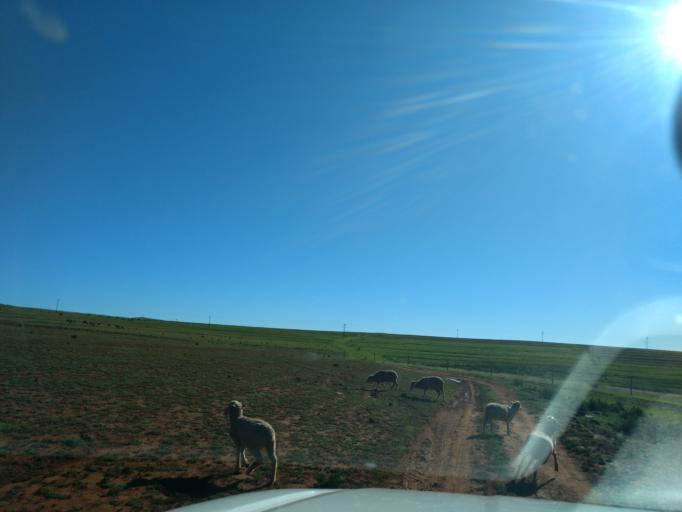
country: LS
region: Berea
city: Teyateyaneng
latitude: -29.3681
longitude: 27.7852
